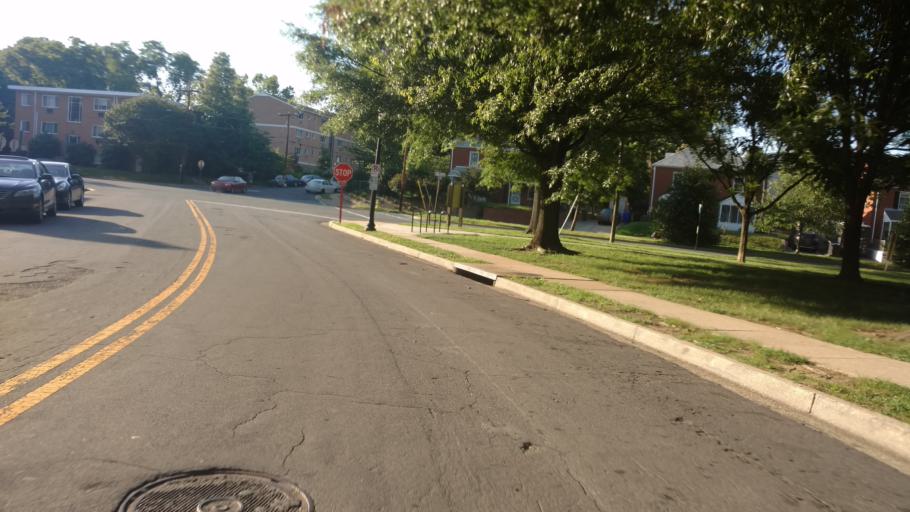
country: US
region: Virginia
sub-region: Arlington County
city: Arlington
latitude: 38.8683
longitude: -77.0832
